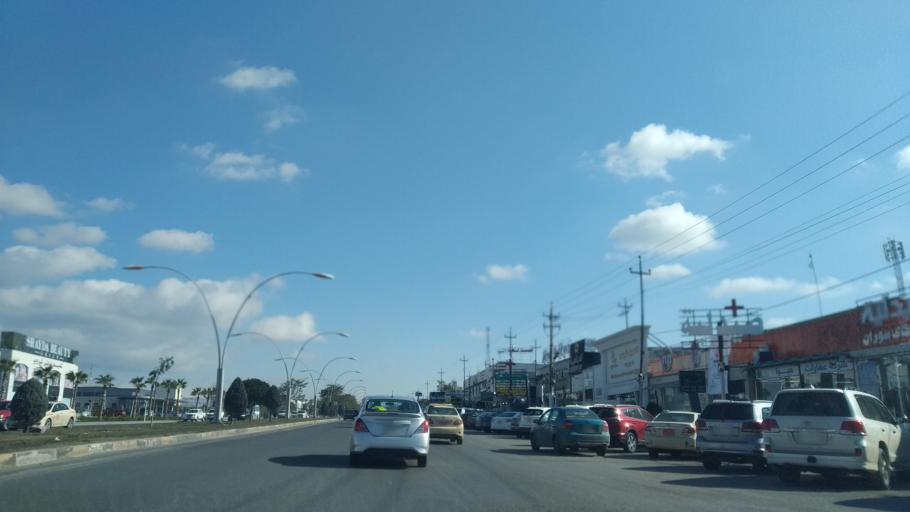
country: IQ
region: Arbil
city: Erbil
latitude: 36.2002
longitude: 44.0900
